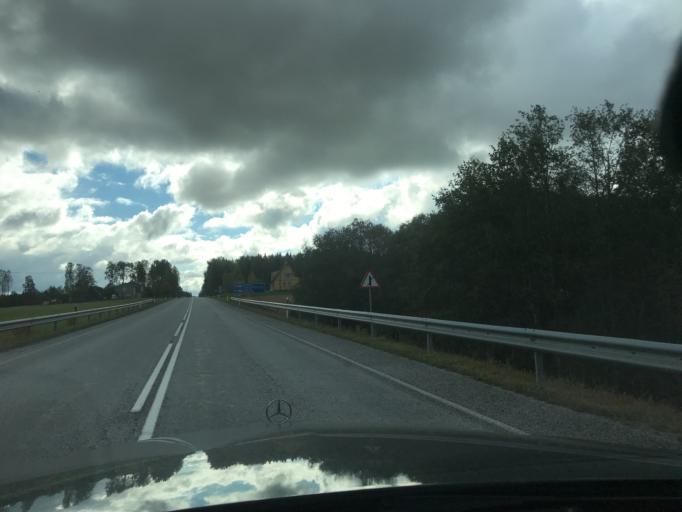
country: RU
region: Pskov
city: Pechory
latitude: 57.7162
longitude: 27.3188
